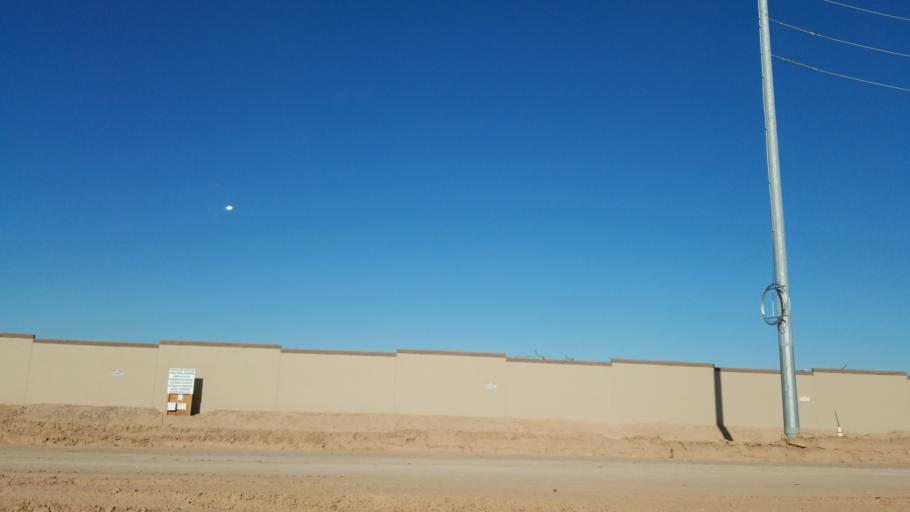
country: US
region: Arizona
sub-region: Maricopa County
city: Goodyear
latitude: 33.4419
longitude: -112.3755
